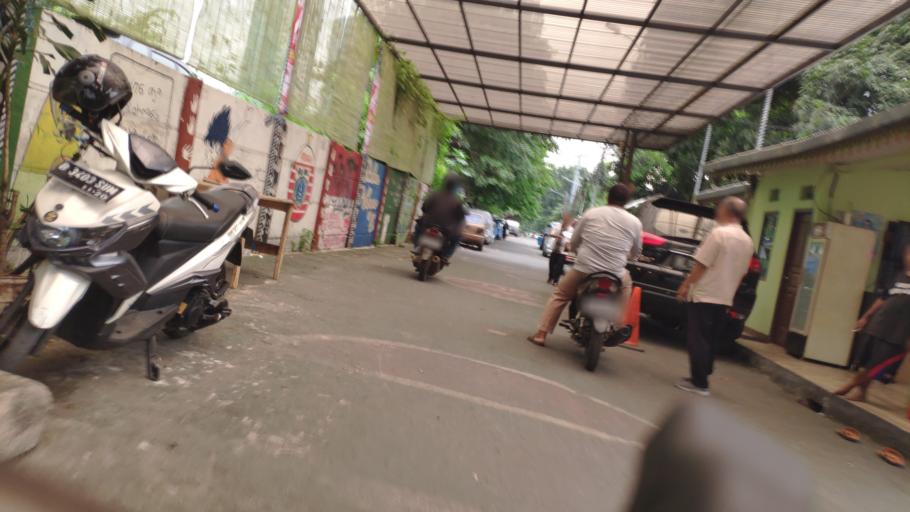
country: ID
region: Jakarta Raya
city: Jakarta
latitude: -6.2117
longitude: 106.8356
